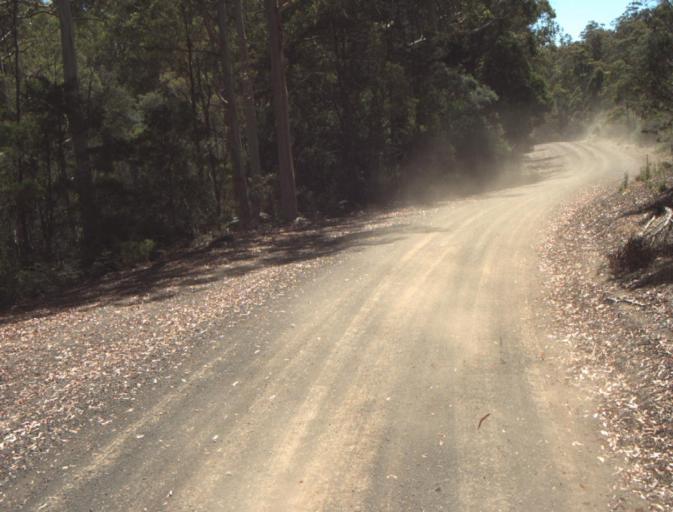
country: AU
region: Tasmania
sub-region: Launceston
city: Newstead
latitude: -41.3019
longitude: 147.3330
